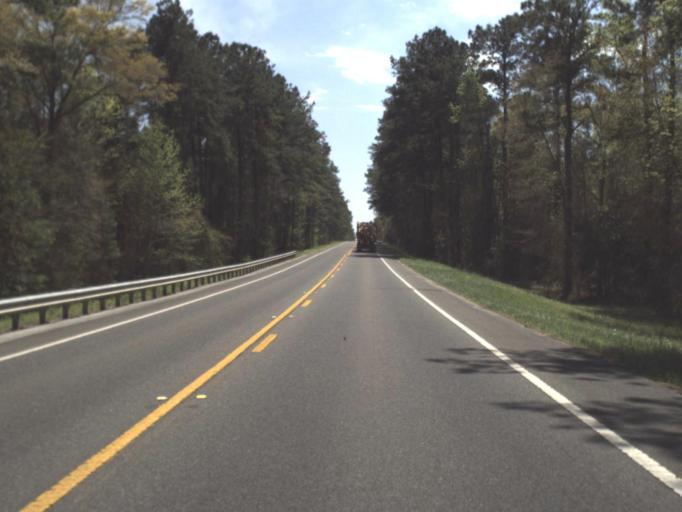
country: US
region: Florida
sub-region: Walton County
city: DeFuniak Springs
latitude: 30.7902
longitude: -85.9586
